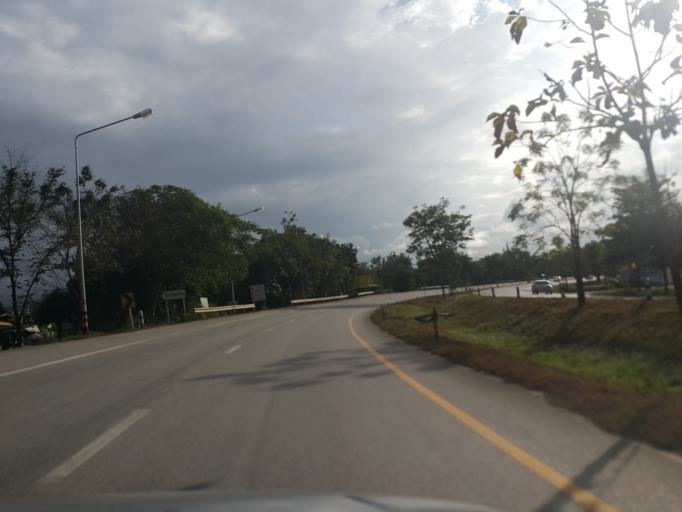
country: TH
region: Lampang
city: Ko Kha
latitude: 18.1489
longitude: 99.4018
